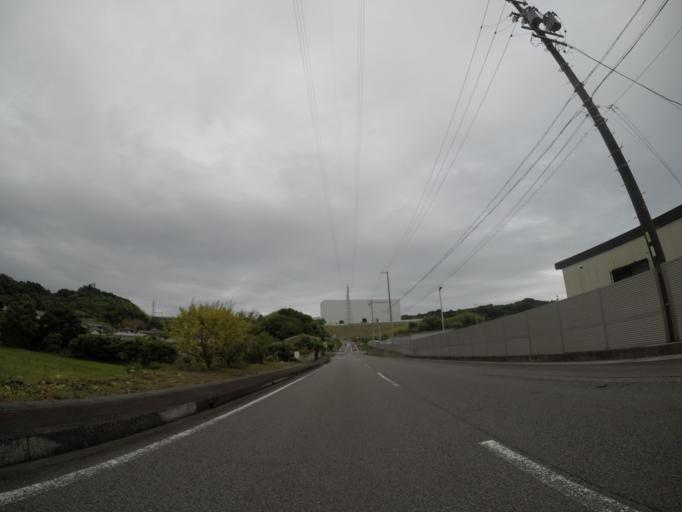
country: JP
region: Shizuoka
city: Sagara
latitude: 34.7298
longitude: 138.1803
